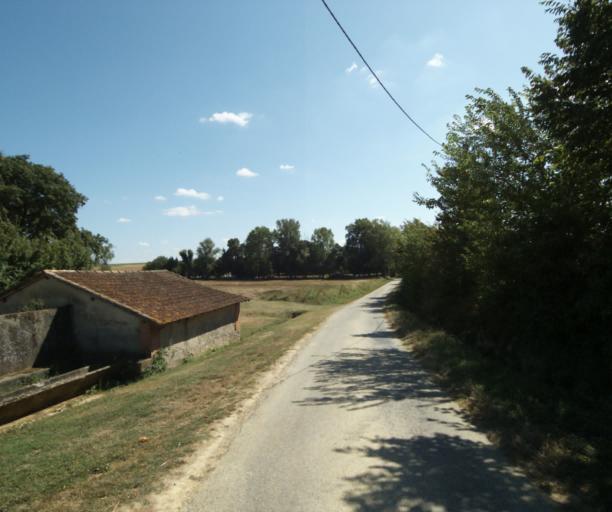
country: FR
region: Midi-Pyrenees
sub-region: Departement de la Haute-Garonne
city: Saint-Felix-Lauragais
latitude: 43.4844
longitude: 1.8987
